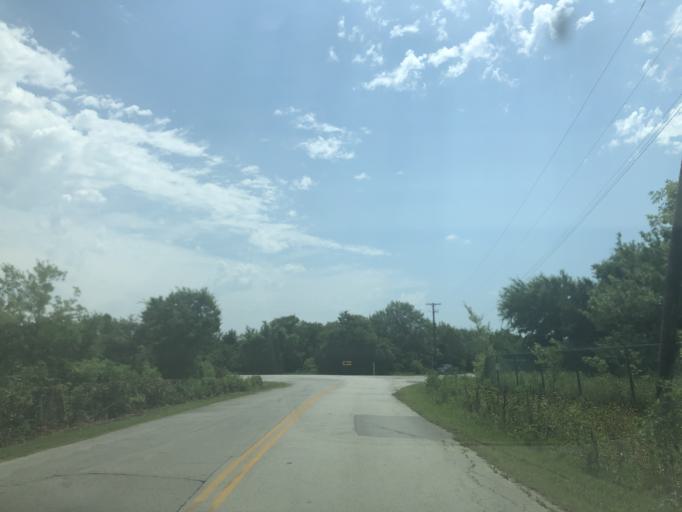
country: US
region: Texas
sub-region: Dallas County
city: Irving
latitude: 32.7866
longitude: -96.9350
